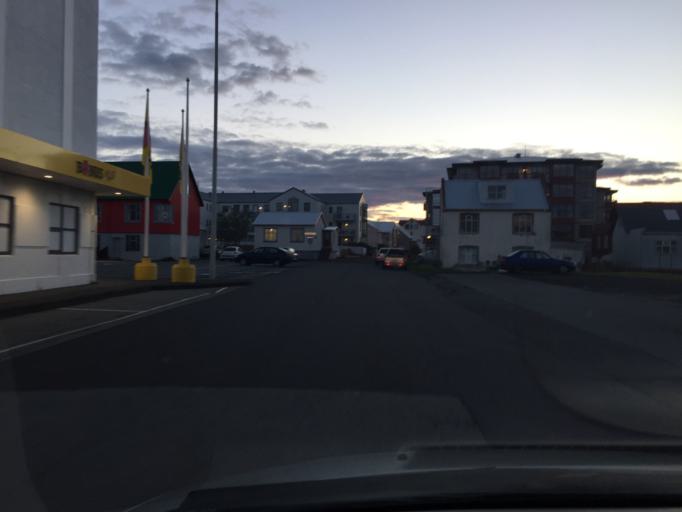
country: IS
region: Southern Peninsula
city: Reykjanesbaer
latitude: 64.0033
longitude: -22.5563
